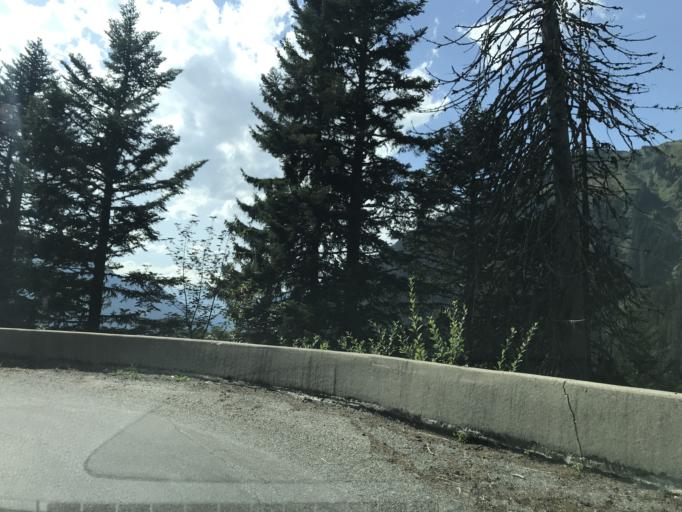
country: FR
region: Rhone-Alpes
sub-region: Departement de la Savoie
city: Beaufort
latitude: 45.7071
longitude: 6.6331
